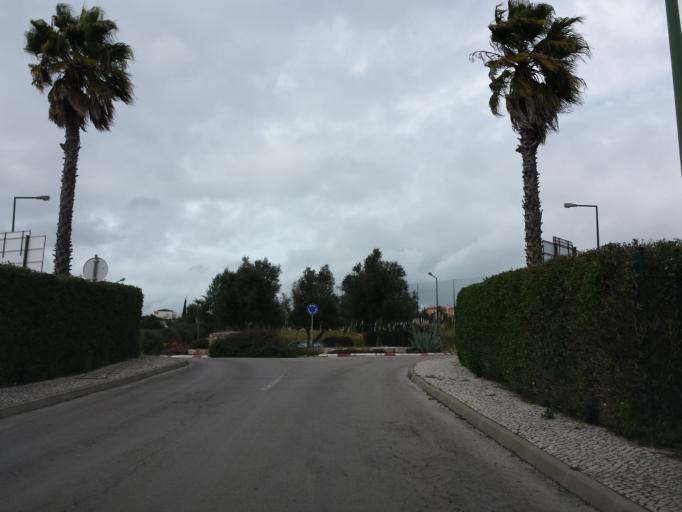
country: PT
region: Faro
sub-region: Lagoa
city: Estombar
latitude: 37.1332
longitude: -8.4810
